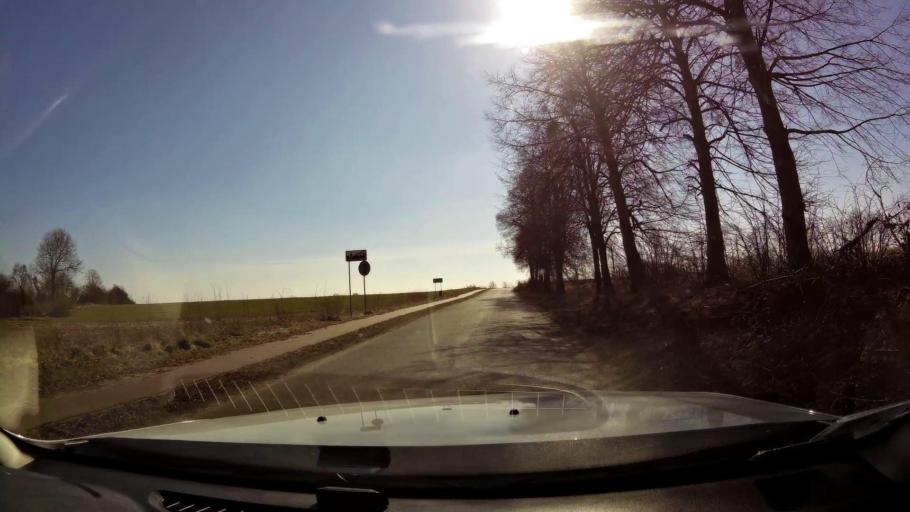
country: PL
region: West Pomeranian Voivodeship
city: Trzcinsko Zdroj
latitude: 52.9835
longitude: 14.6071
